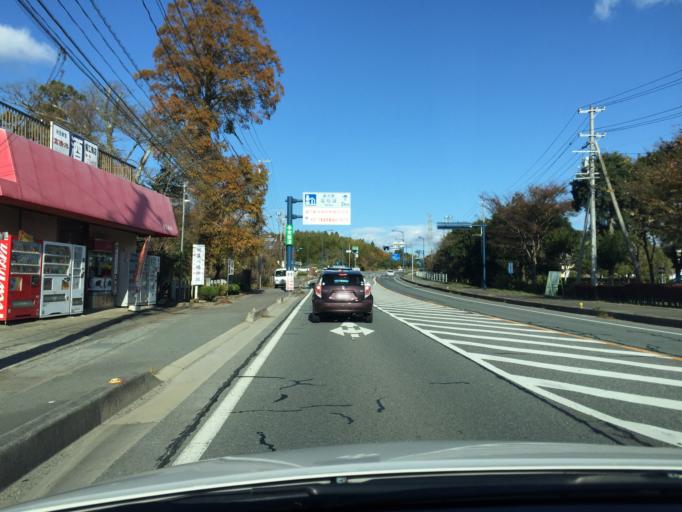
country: JP
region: Fukushima
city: Iwaki
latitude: 37.2320
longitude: 140.9995
